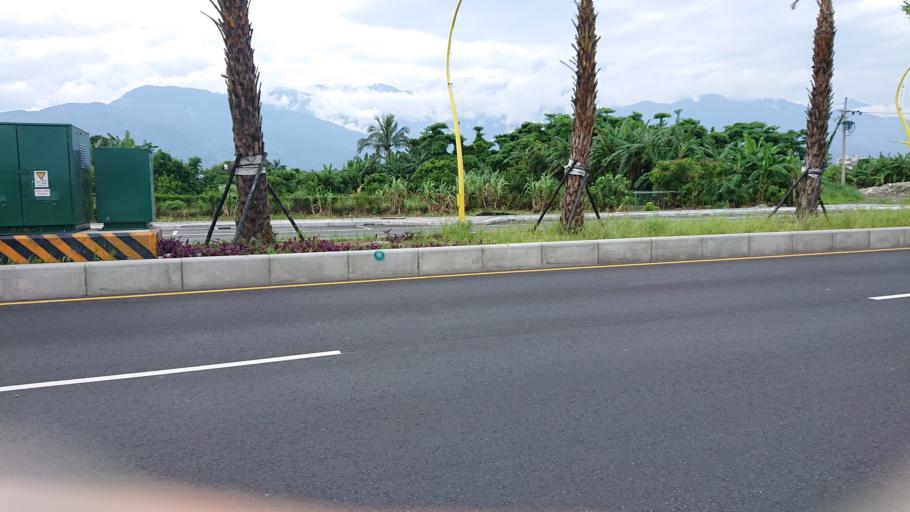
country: TW
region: Taiwan
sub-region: Hualien
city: Hualian
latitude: 23.9536
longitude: 121.6007
